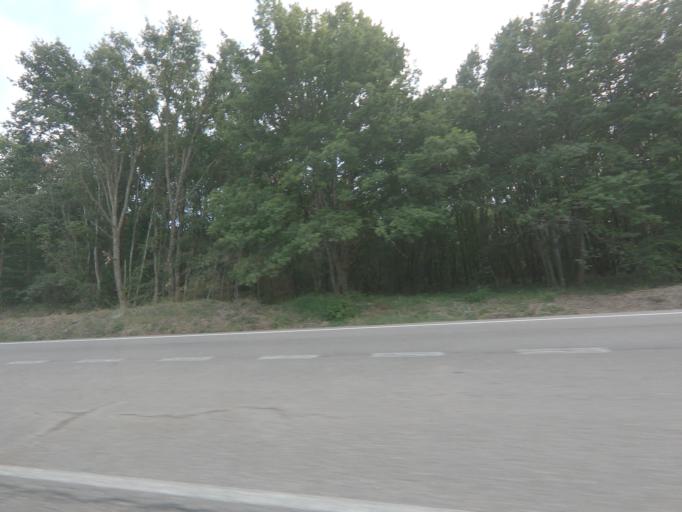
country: ES
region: Galicia
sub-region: Provincia de Ourense
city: Taboadela
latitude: 42.2201
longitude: -7.8411
